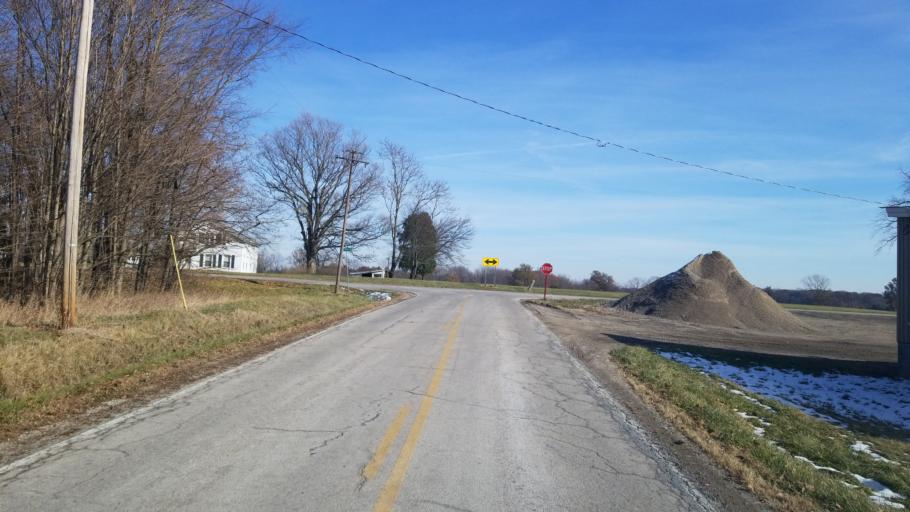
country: US
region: Ohio
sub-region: Huron County
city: Wakeman
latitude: 41.1976
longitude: -82.4570
